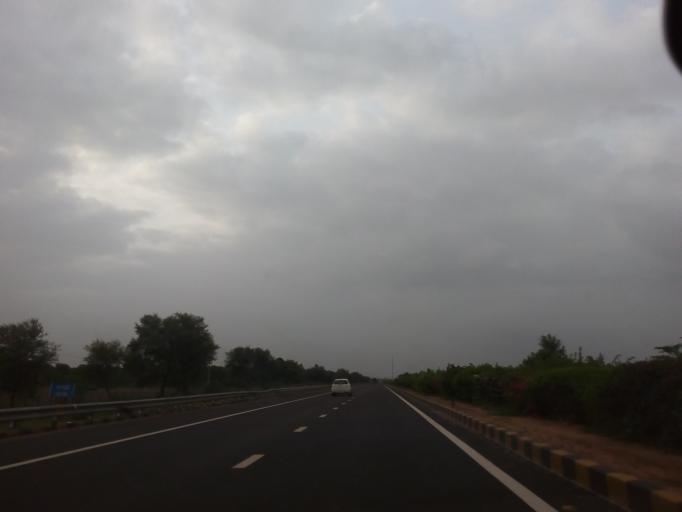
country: IN
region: Gujarat
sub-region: Kheda
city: Mahemdavad
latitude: 22.8877
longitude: 72.7886
